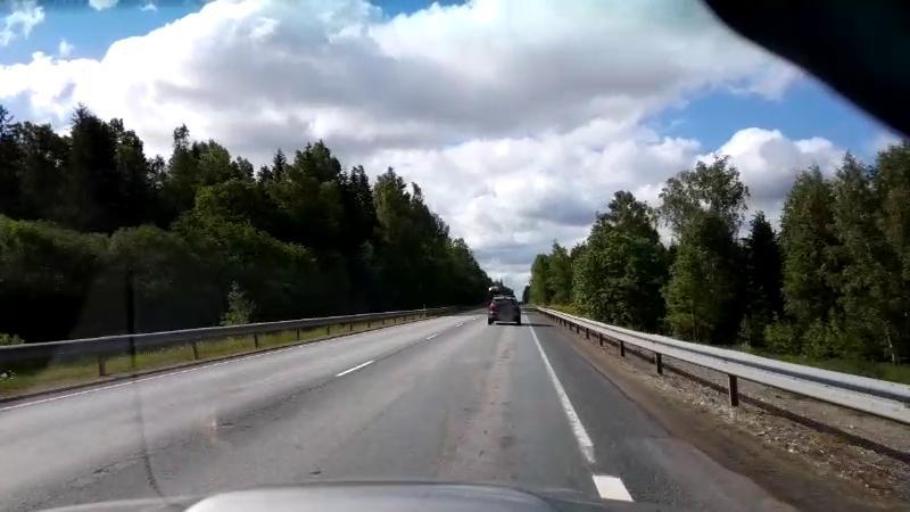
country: EE
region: Harju
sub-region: Saue linn
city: Saue
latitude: 59.2160
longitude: 24.4954
